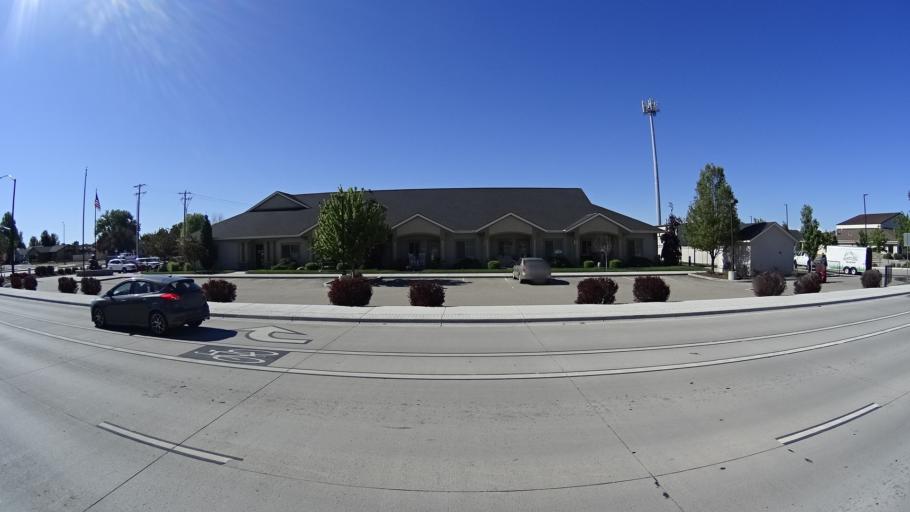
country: US
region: Idaho
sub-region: Ada County
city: Meridian
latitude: 43.6336
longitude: -116.3945
